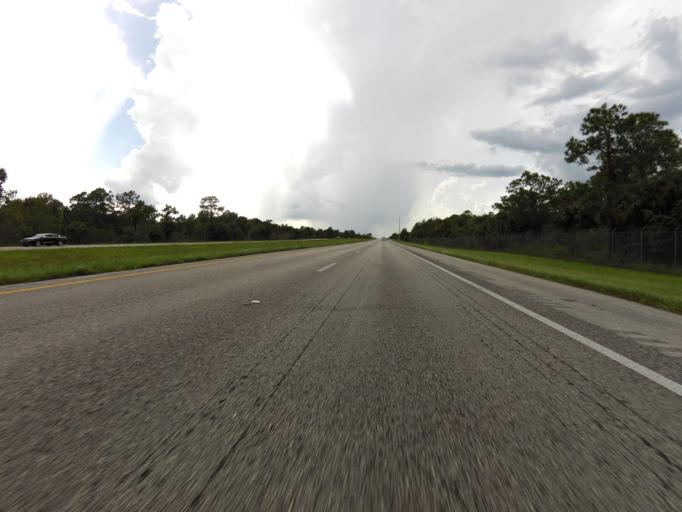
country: US
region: Florida
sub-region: Collier County
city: Orangetree
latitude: 26.1534
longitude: -81.4637
